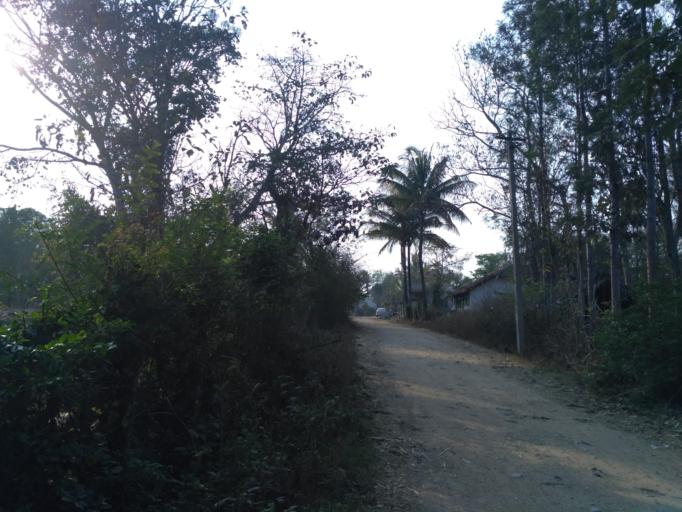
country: IN
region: Karnataka
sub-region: Hassan
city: Alur
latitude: 12.9918
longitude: 76.0230
